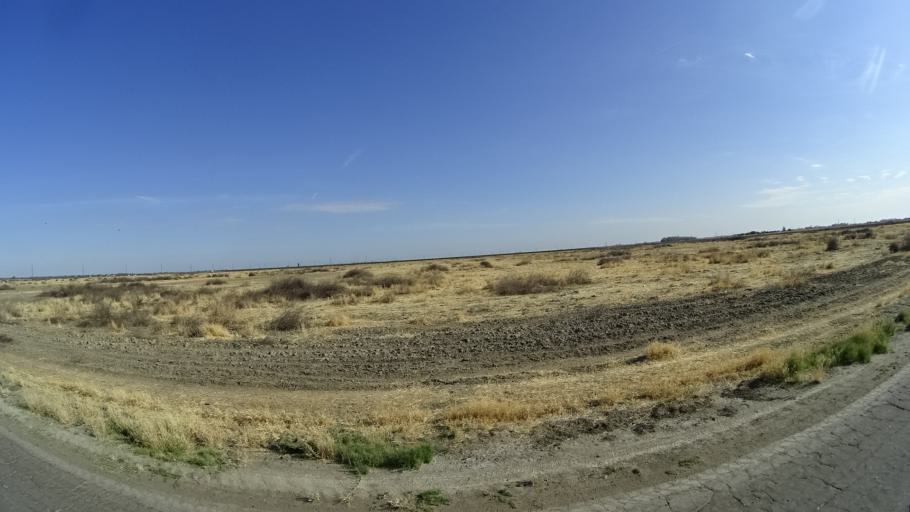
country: US
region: California
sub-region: Kings County
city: Stratford
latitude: 36.2261
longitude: -119.8293
